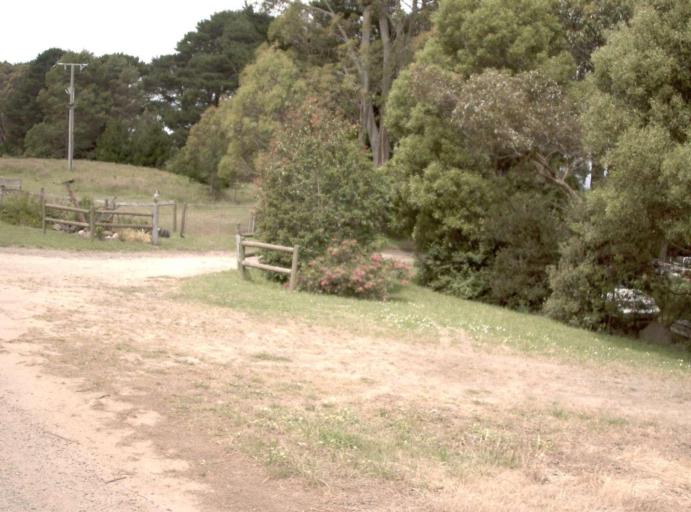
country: AU
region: Victoria
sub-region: Latrobe
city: Traralgon
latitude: -38.3733
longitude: 146.6869
